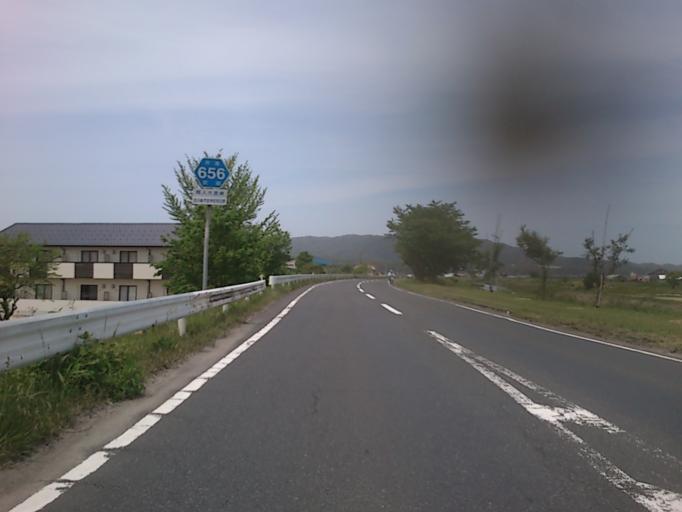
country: JP
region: Kyoto
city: Miyazu
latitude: 35.6598
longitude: 135.0869
